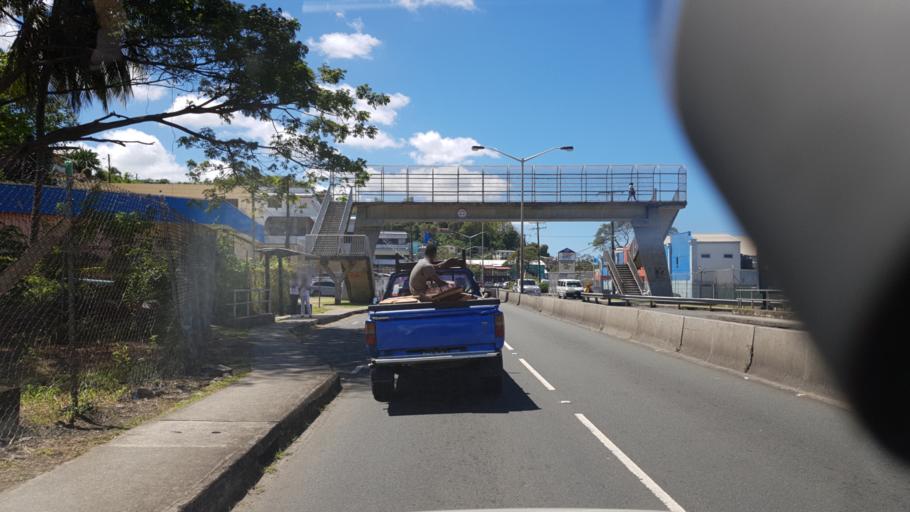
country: LC
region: Castries Quarter
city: Bisee
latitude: 14.0255
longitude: -60.9790
